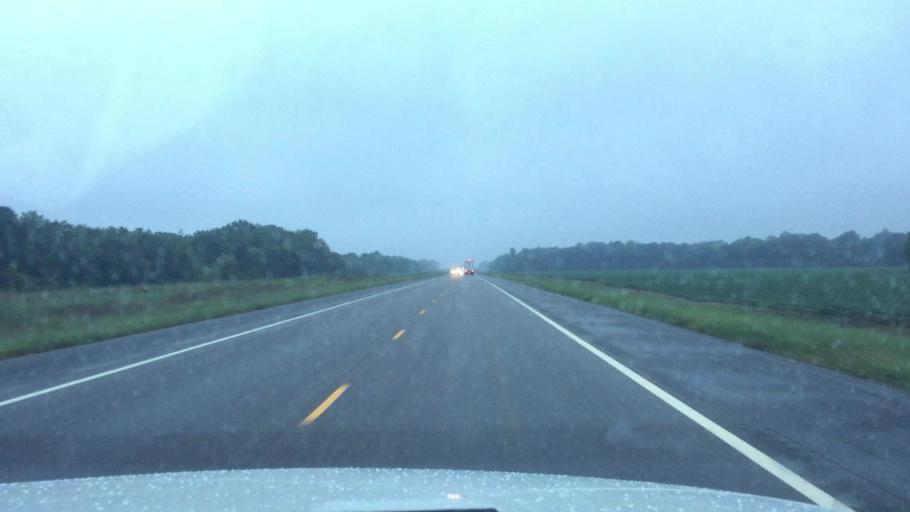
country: US
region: Kansas
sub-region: Montgomery County
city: Cherryvale
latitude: 37.4224
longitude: -95.4939
